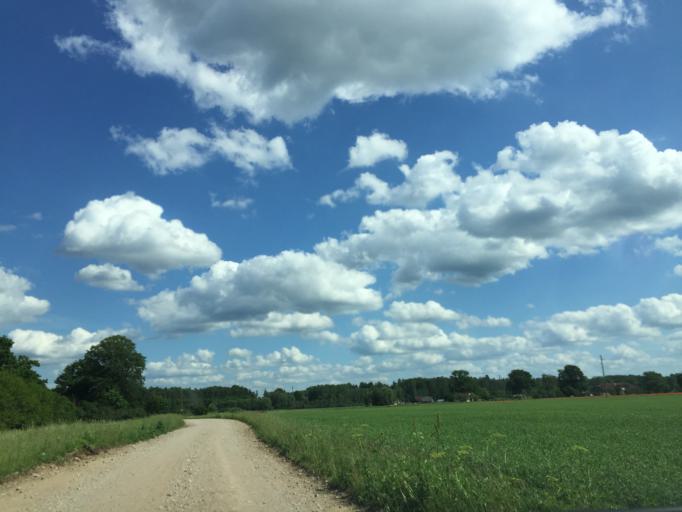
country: LV
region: Engure
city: Smarde
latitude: 56.8172
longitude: 23.3794
